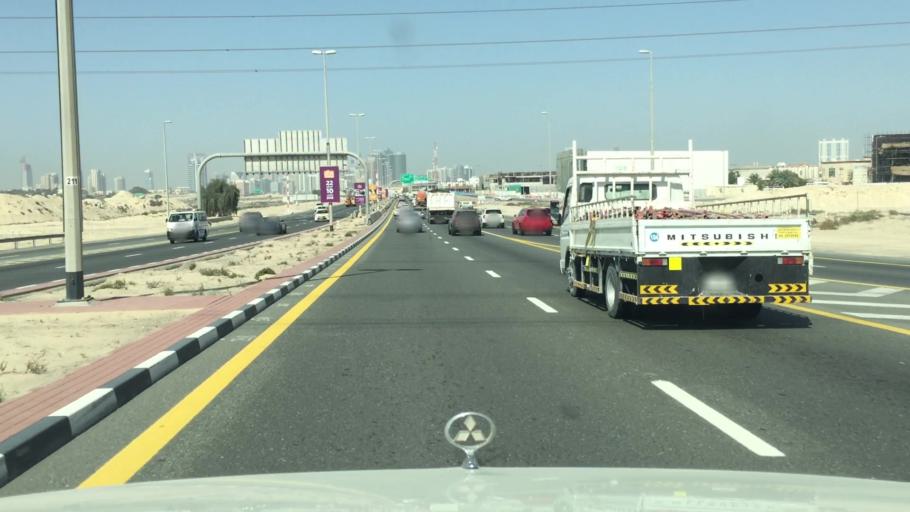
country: AE
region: Dubai
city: Dubai
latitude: 25.0785
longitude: 55.2083
